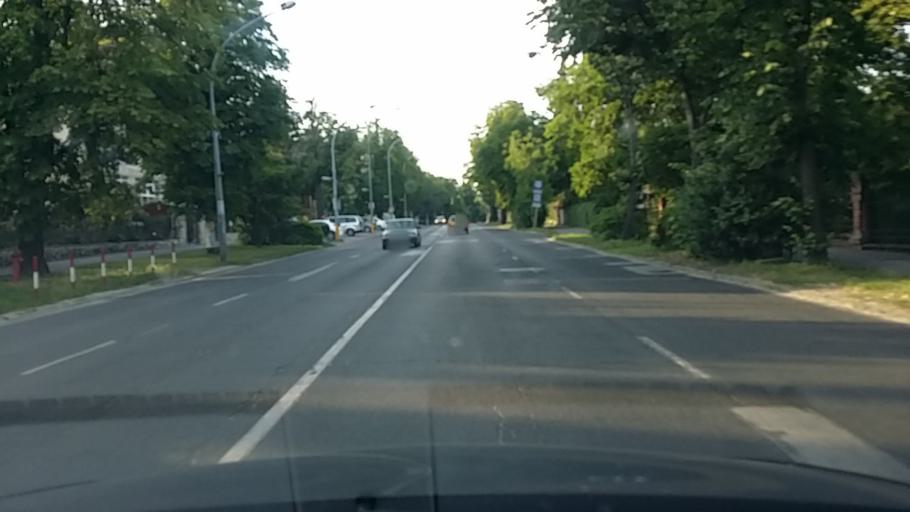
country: HU
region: Borsod-Abauj-Zemplen
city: Miskolc
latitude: 48.0923
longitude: 20.7858
